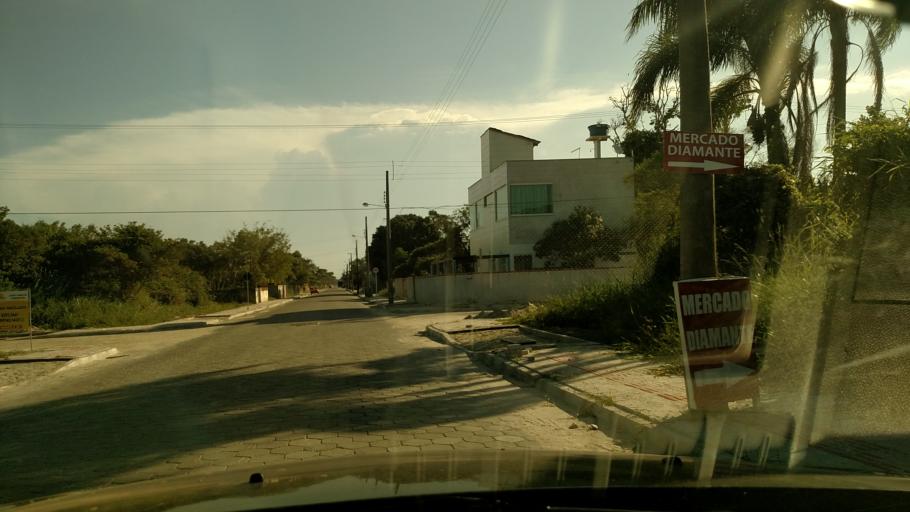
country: BR
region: Santa Catarina
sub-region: Porto Belo
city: Porto Belo
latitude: -27.1734
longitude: -48.5038
